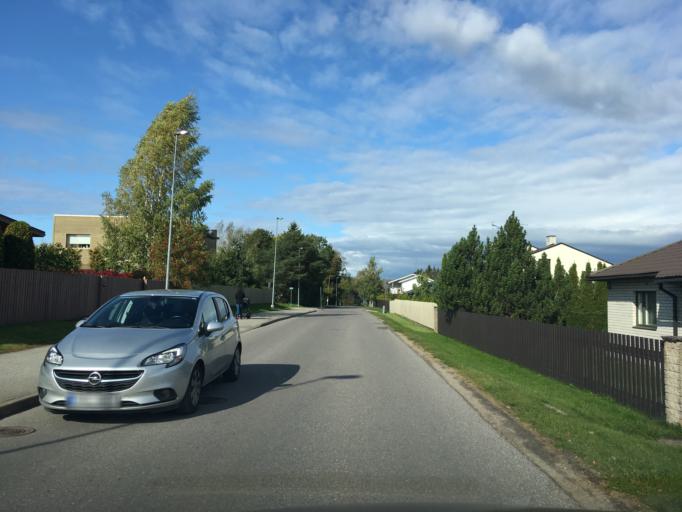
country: EE
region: Harju
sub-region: Saue vald
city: Laagri
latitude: 59.3485
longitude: 24.6395
